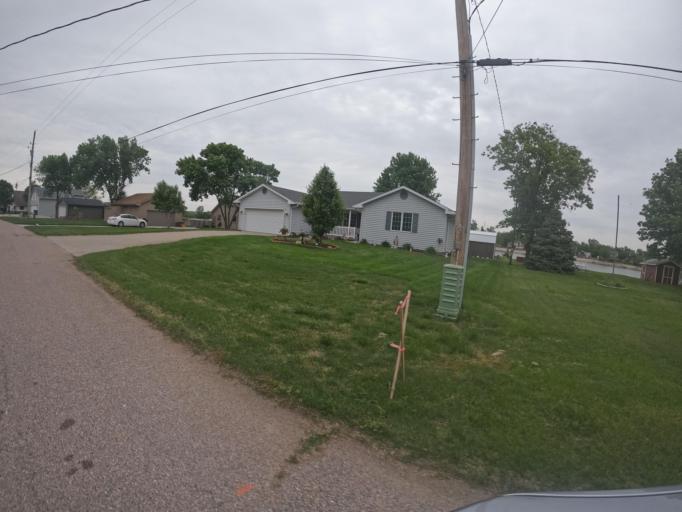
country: US
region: Nebraska
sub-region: Sarpy County
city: Offutt Air Force Base
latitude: 41.0530
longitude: -95.9547
